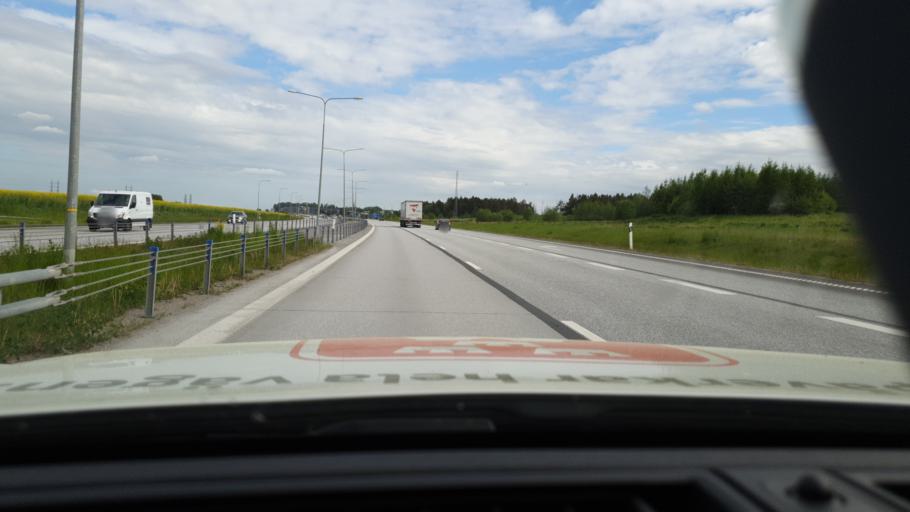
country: SE
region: Uppsala
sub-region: Uppsala Kommun
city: Gamla Uppsala
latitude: 59.8940
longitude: 17.6587
